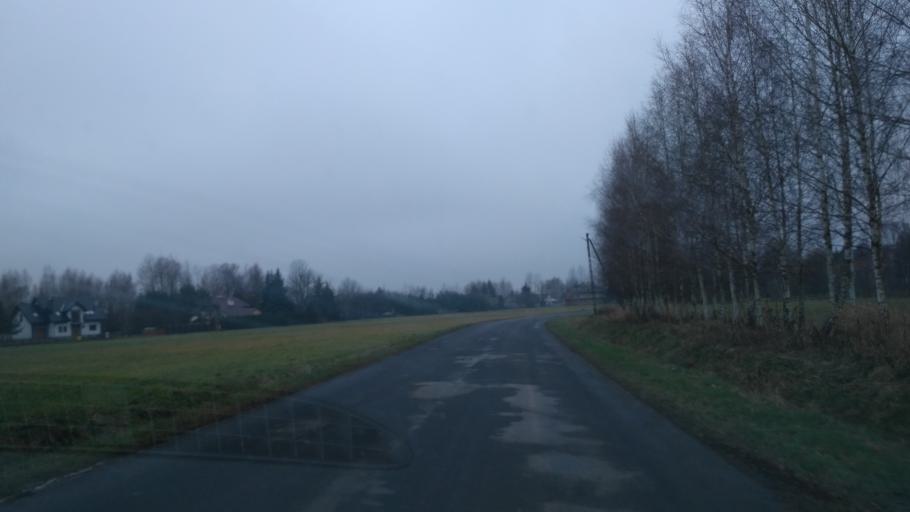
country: PL
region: Subcarpathian Voivodeship
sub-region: Powiat przeworski
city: Zarzecze
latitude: 49.9528
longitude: 22.5676
